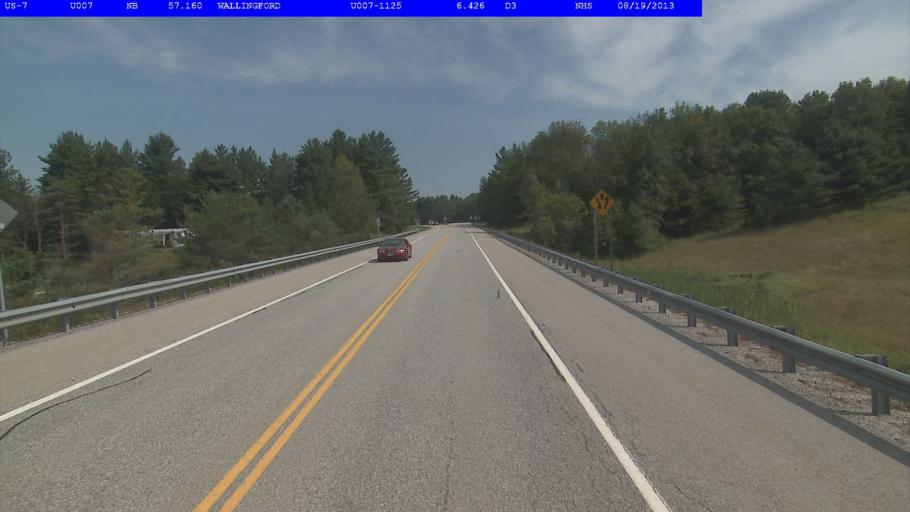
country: US
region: Vermont
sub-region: Rutland County
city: Rutland
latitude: 43.4848
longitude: -72.9728
